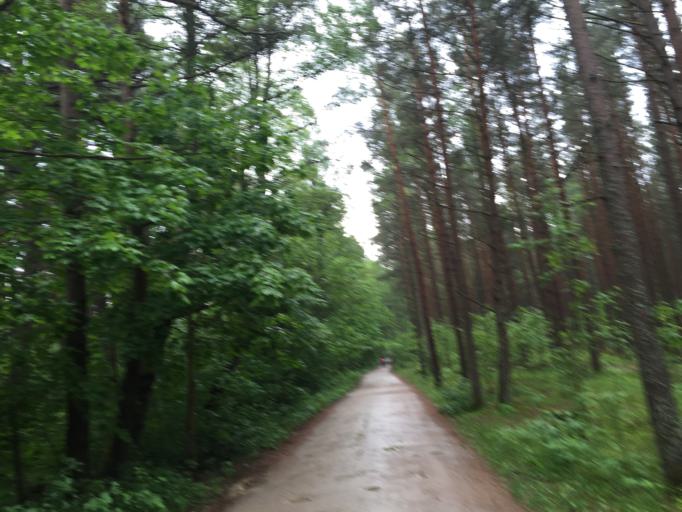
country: LT
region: Klaipedos apskritis
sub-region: Klaipeda
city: Klaipeda
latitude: 55.7984
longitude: 21.0708
